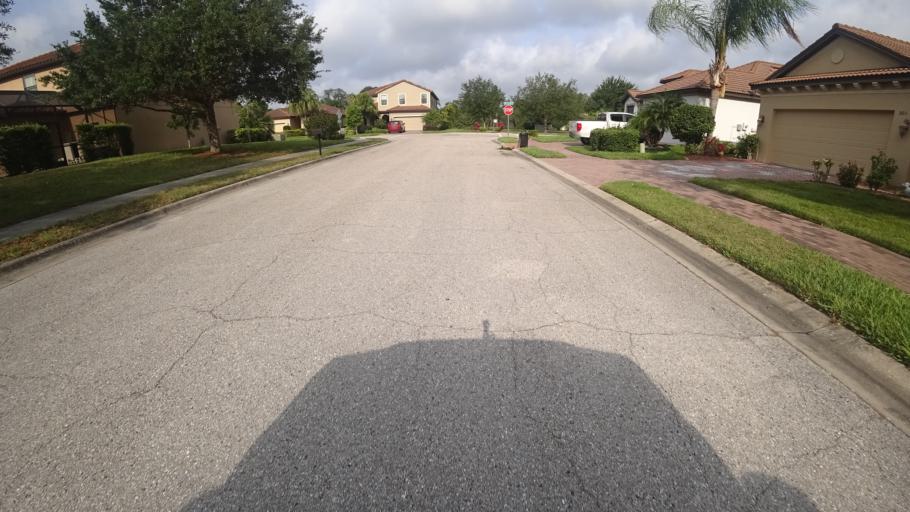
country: US
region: Florida
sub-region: Sarasota County
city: North Sarasota
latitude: 27.3960
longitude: -82.5175
